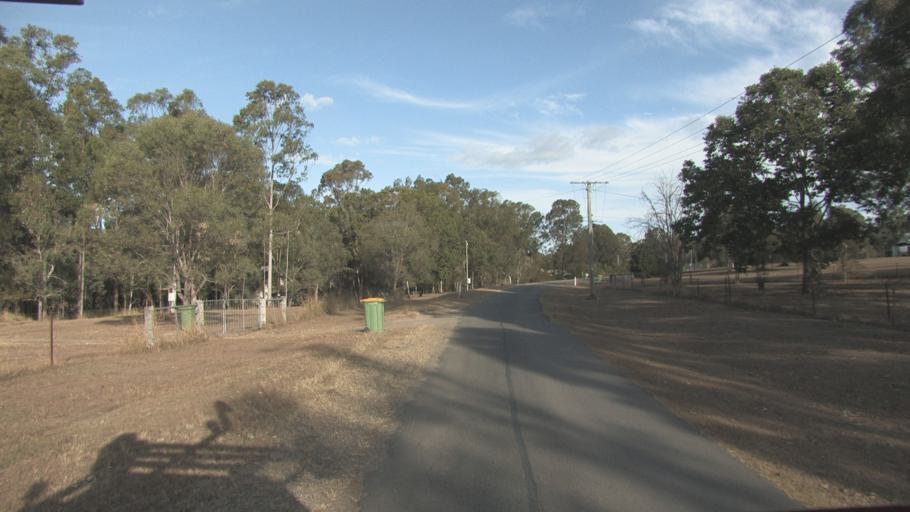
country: AU
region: Queensland
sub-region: Logan
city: Cedar Vale
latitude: -27.8786
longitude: 153.0209
